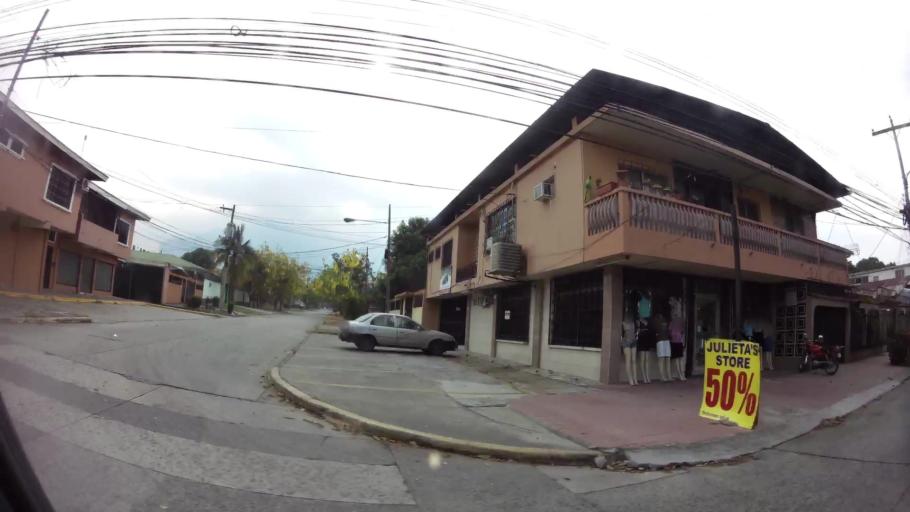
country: HN
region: Cortes
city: San Pedro Sula
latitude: 15.5154
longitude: -88.0259
